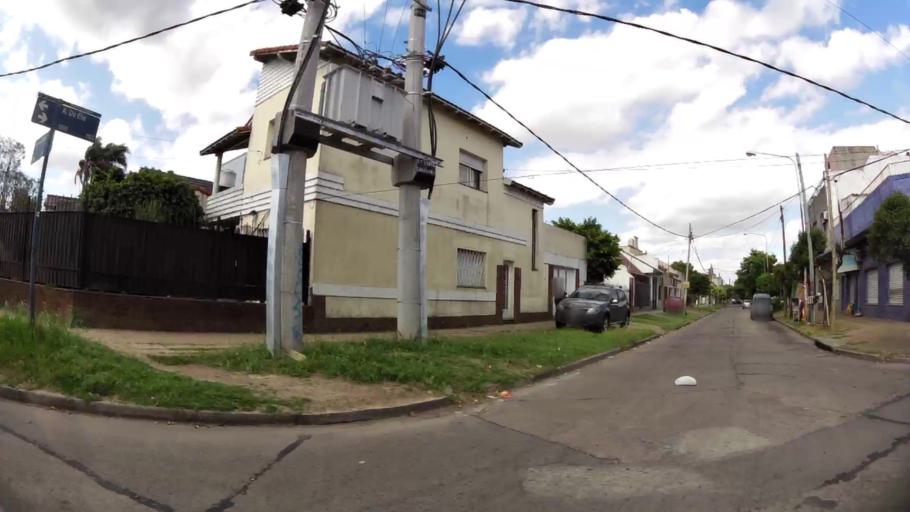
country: AR
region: Buenos Aires
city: San Justo
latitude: -34.6584
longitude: -58.5658
